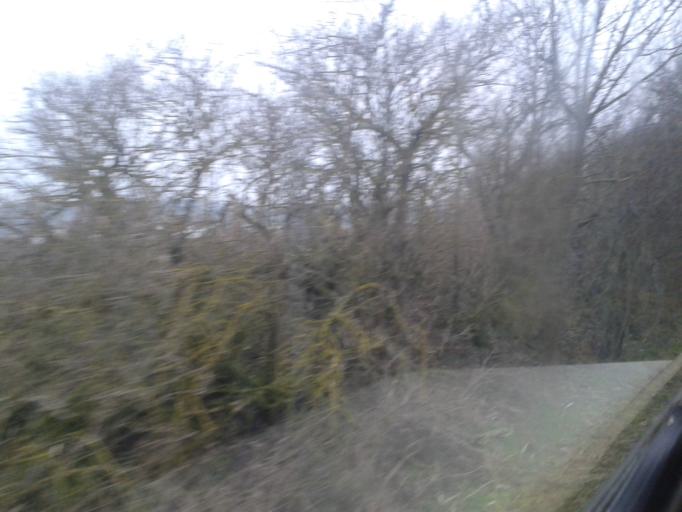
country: CZ
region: Olomoucky
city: Drahanovice
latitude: 49.5786
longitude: 17.0846
